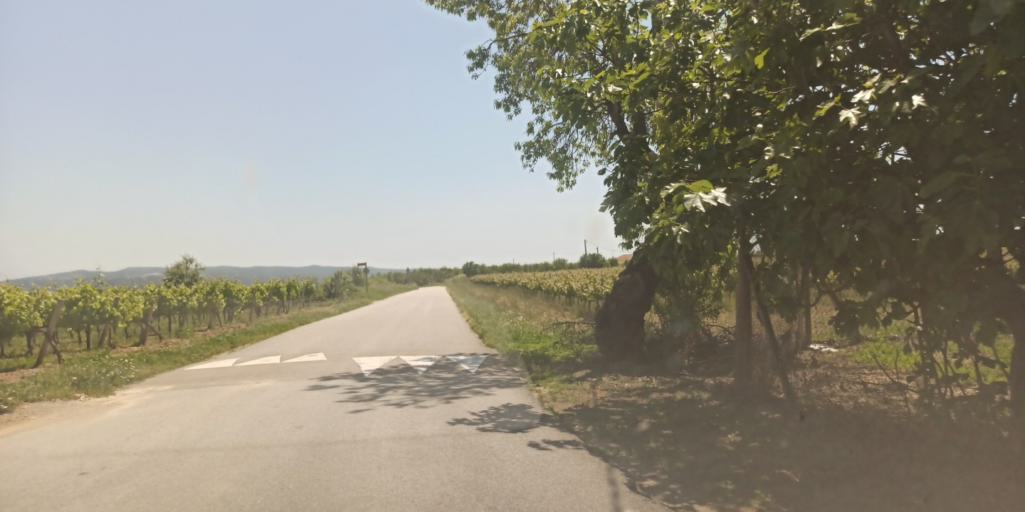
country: ES
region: Catalonia
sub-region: Provincia de Barcelona
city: Vilobi del Penedes
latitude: 41.3682
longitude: 1.6396
